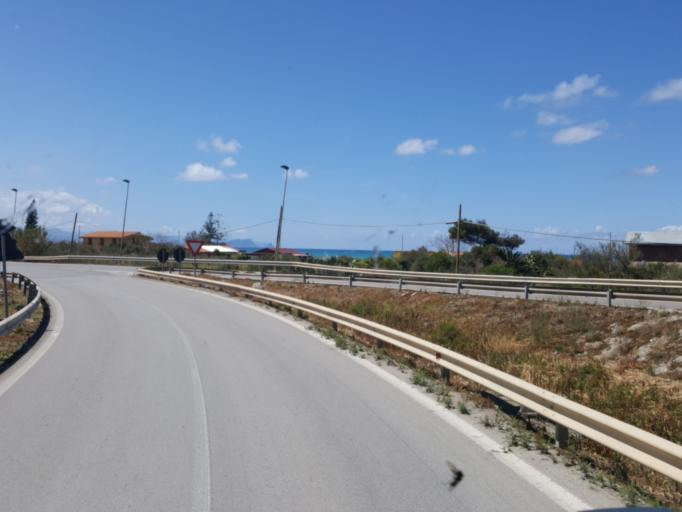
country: IT
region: Sicily
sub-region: Palermo
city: Cerda
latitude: 37.9756
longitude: 13.8076
